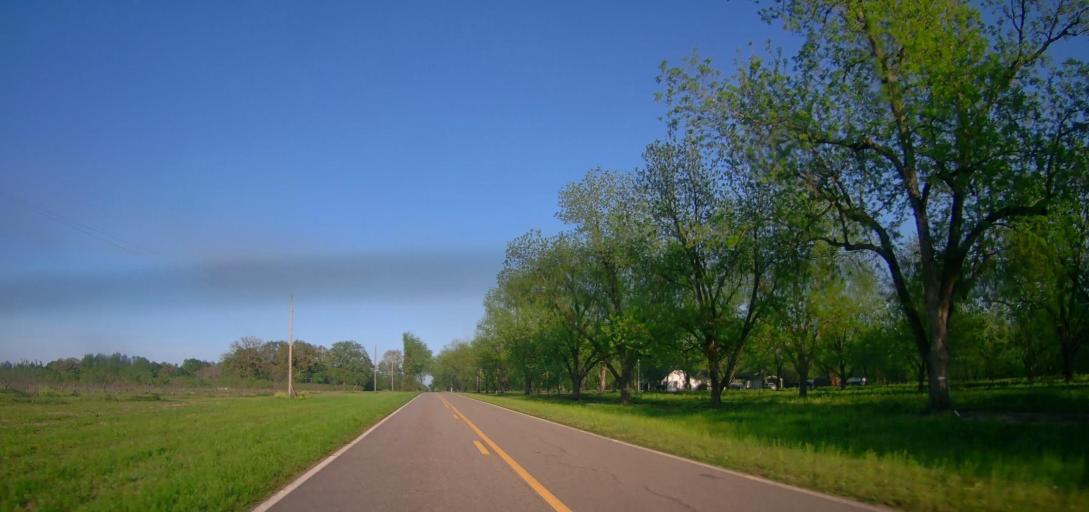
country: US
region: Georgia
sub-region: Macon County
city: Oglethorpe
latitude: 32.3018
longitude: -84.0927
